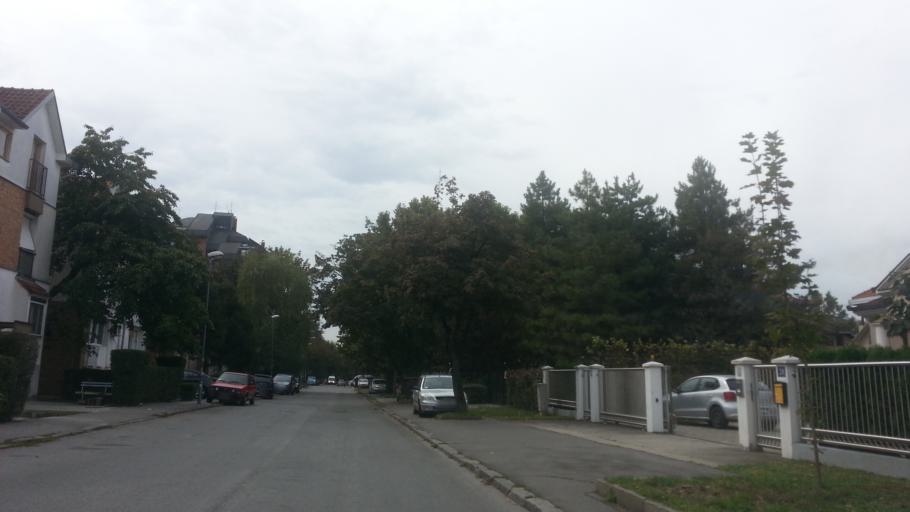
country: RS
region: Central Serbia
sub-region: Belgrade
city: Zemun
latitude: 44.8586
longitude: 20.3666
